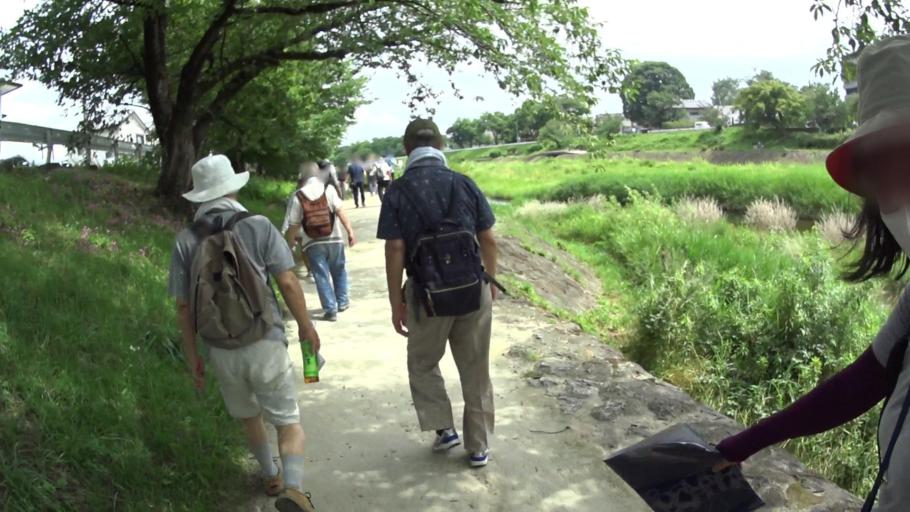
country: JP
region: Kyoto
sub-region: Kyoto-shi
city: Kamigyo-ku
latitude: 35.0529
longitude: 135.7565
